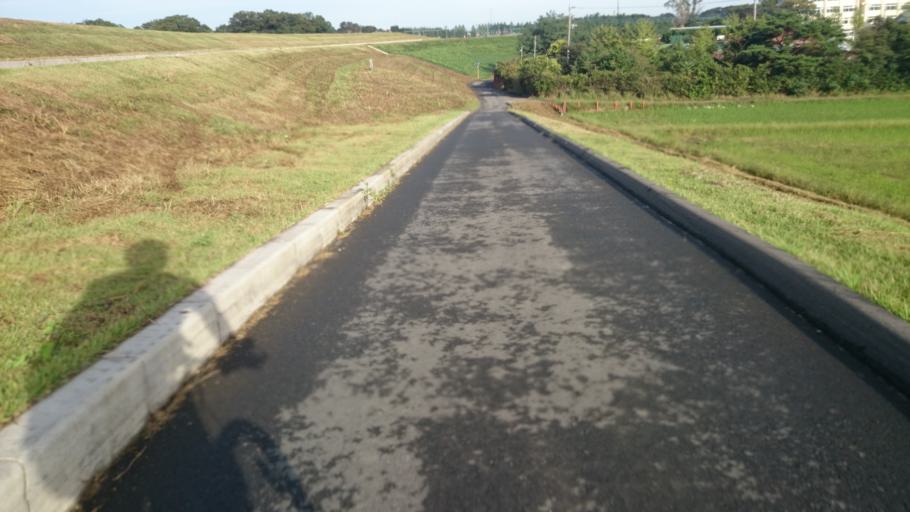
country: JP
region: Saitama
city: Kamifukuoka
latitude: 35.9070
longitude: 139.5608
